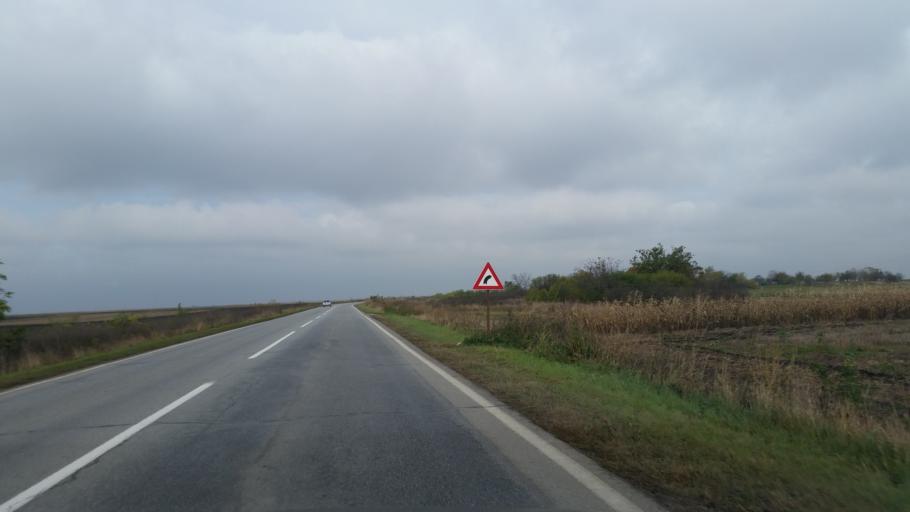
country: RS
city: Elemir
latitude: 45.4661
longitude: 20.3433
